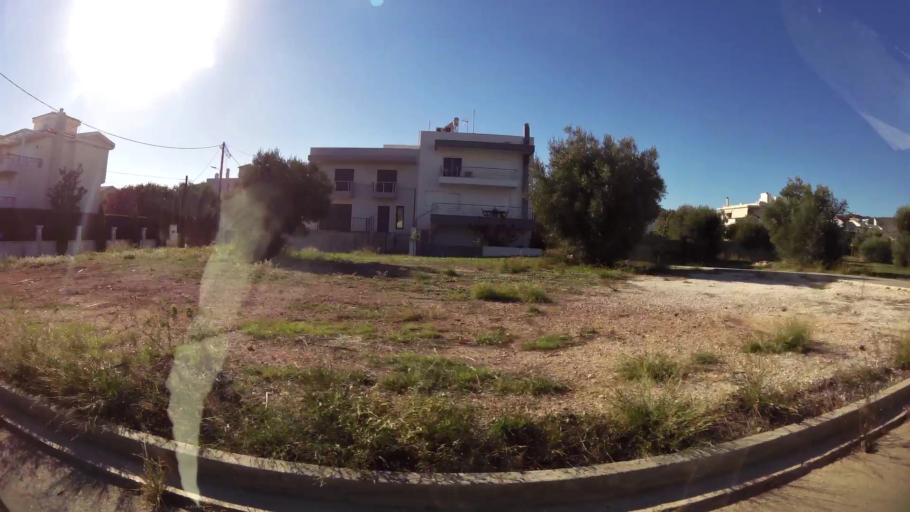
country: GR
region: Attica
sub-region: Nomarchia Anatolikis Attikis
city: Vari
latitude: 37.8330
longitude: 23.8103
